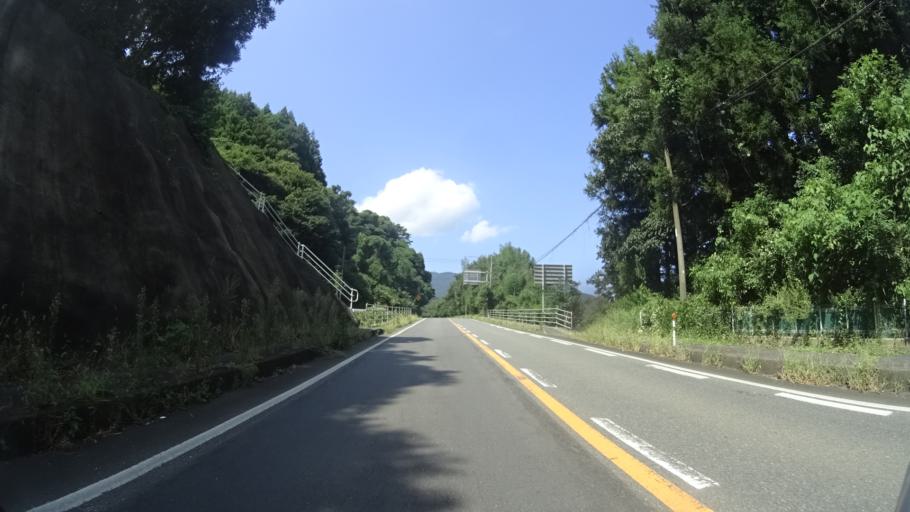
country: JP
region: Shimane
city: Masuda
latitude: 34.6393
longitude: 131.6512
